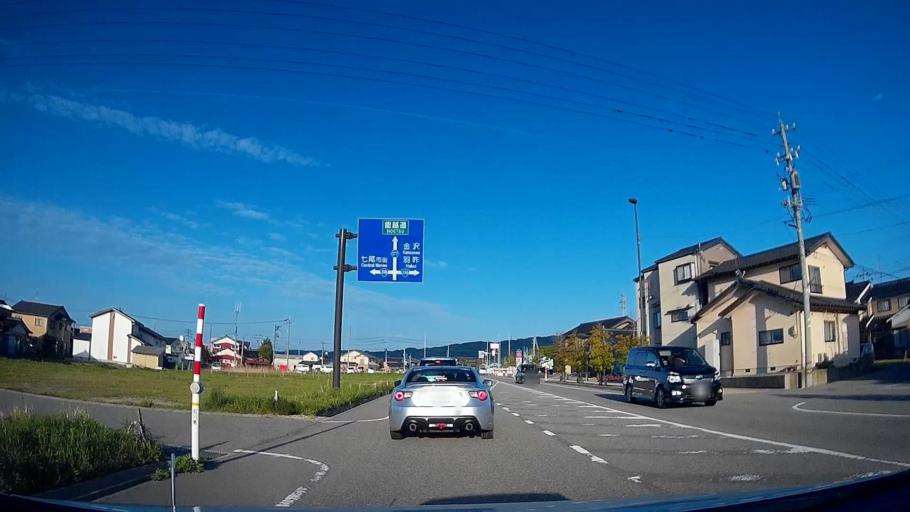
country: JP
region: Ishikawa
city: Nanao
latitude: 37.0320
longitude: 136.9654
